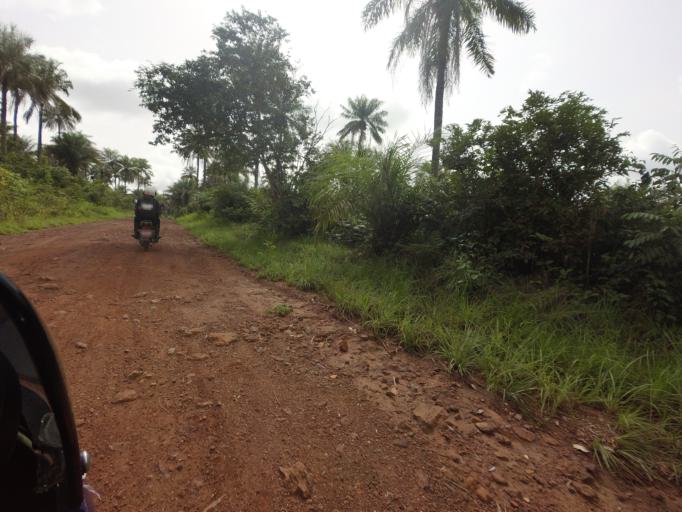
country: SL
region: Northern Province
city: Kambia
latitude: 9.1031
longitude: -12.9898
